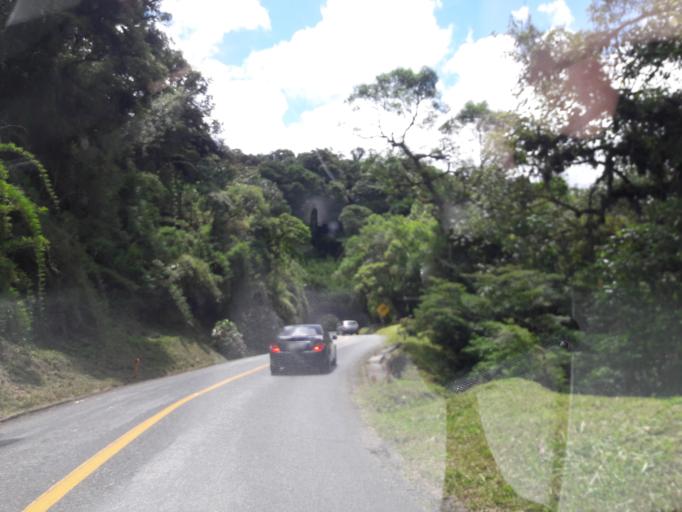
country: BR
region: Parana
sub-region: Campina Grande Do Sul
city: Campina Grande do Sul
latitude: -25.3312
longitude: -48.9003
